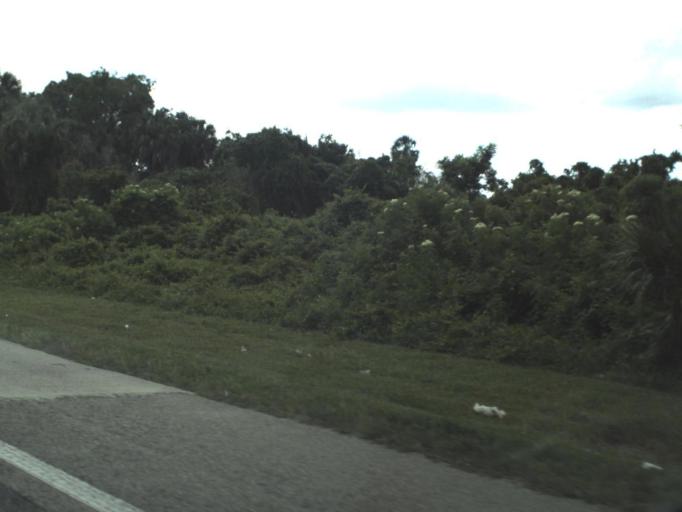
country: US
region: Florida
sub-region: Brevard County
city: Cocoa
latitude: 28.4054
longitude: -80.7160
